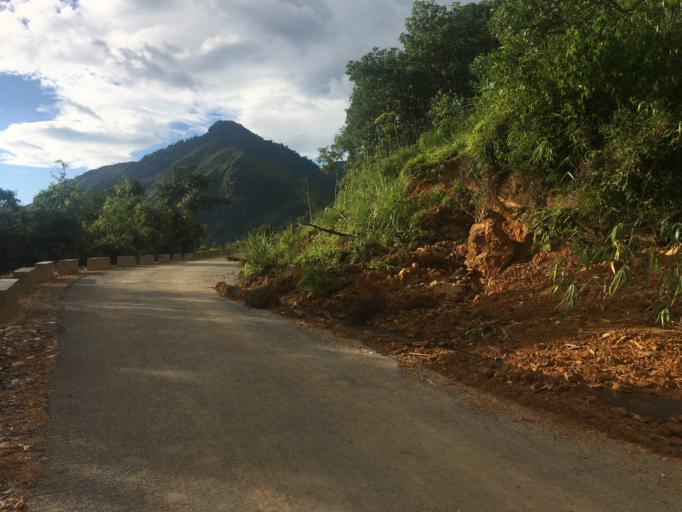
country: VN
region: Ha Giang
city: Thi Tran Tam Son
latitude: 22.9486
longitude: 105.0256
